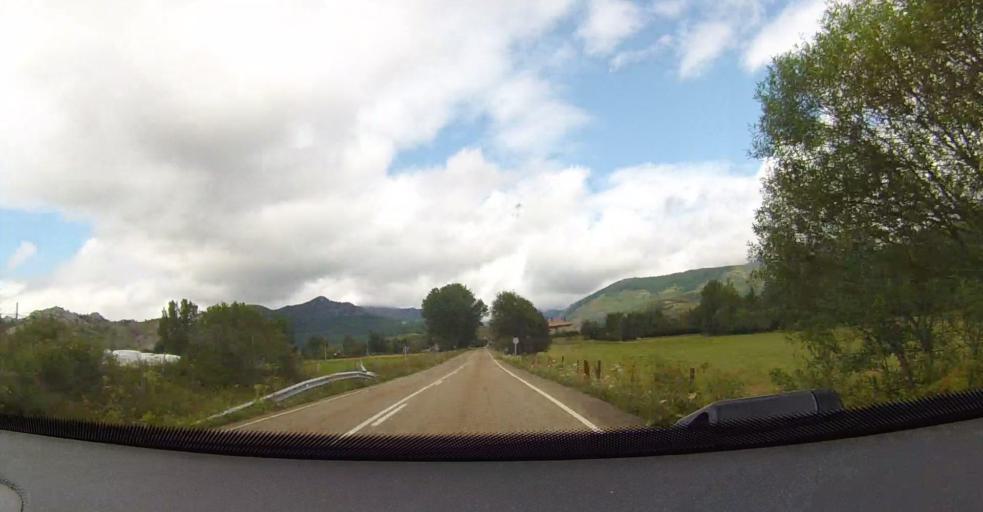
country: ES
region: Castille and Leon
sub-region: Provincia de Leon
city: Puebla de Lillo
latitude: 42.9989
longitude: -5.2656
